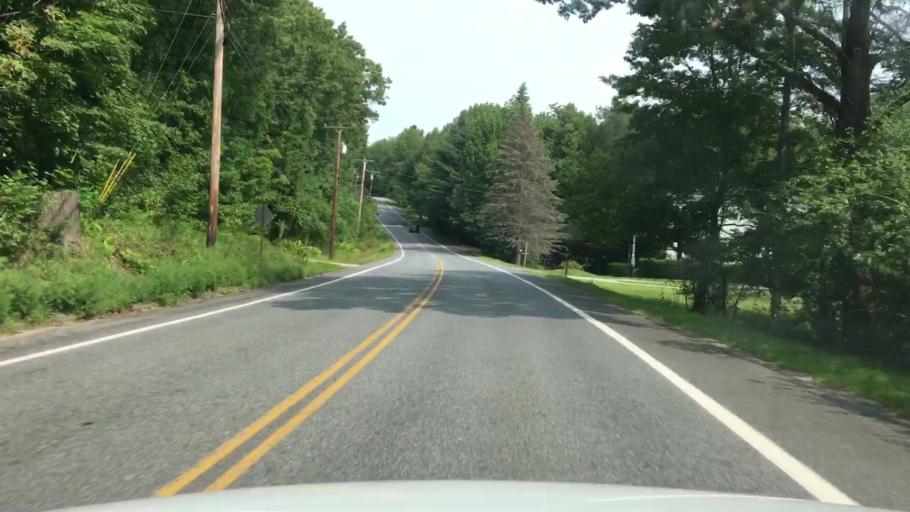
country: US
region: Maine
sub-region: Kennebec County
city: Winthrop
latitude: 44.3160
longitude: -69.9776
